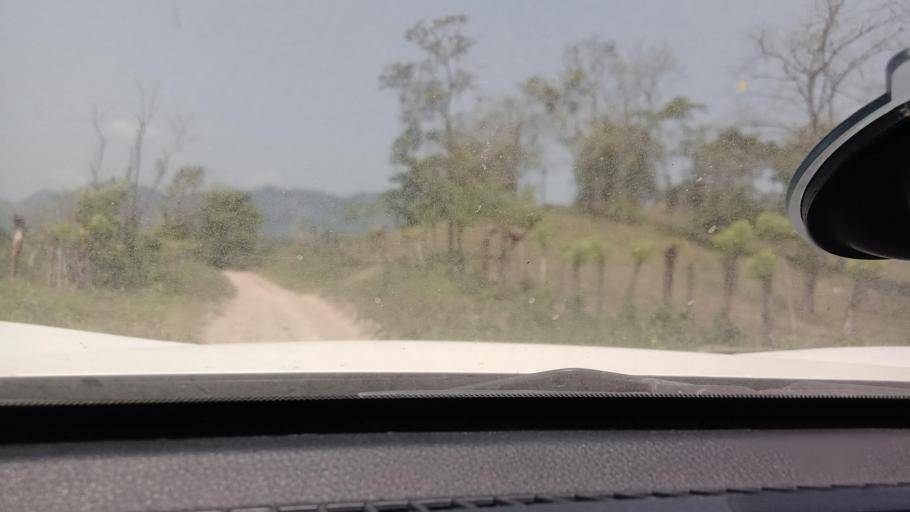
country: MX
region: Tabasco
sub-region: Huimanguillo
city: Francisco Rueda
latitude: 17.4851
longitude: -93.9359
